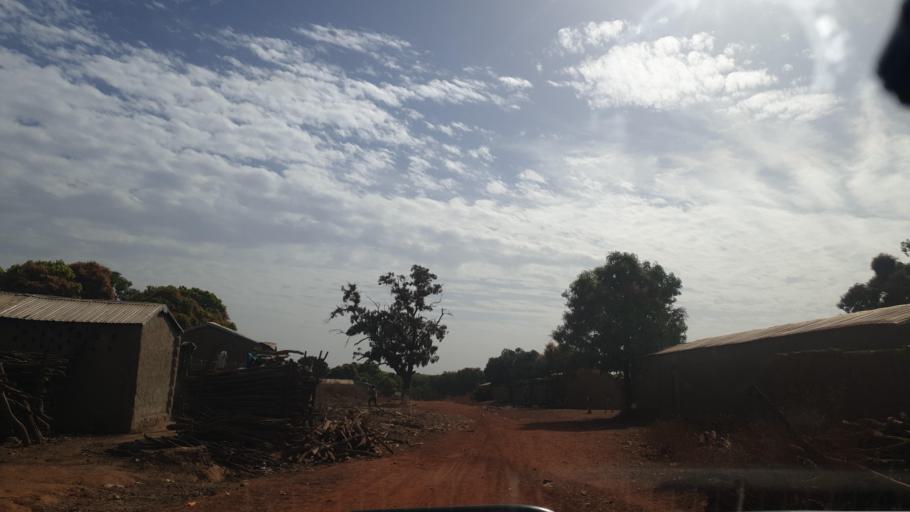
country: ML
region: Sikasso
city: Yanfolila
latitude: 11.4185
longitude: -7.9949
